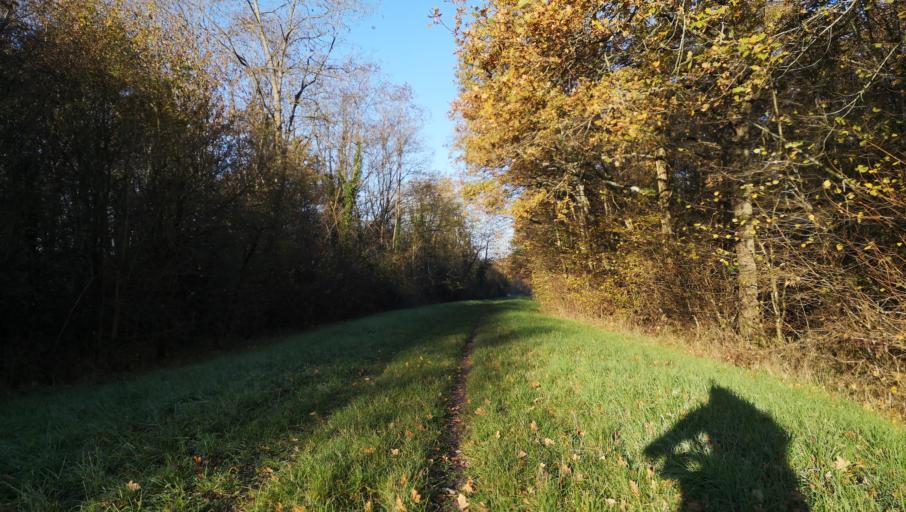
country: FR
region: Centre
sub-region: Departement du Loiret
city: Saran
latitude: 47.9436
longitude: 1.8605
